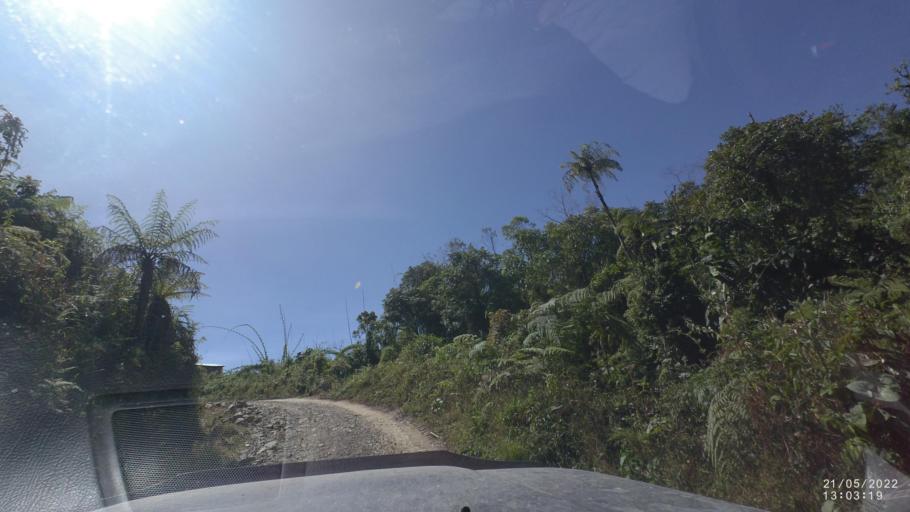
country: BO
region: Cochabamba
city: Colomi
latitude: -17.1595
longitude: -65.9523
